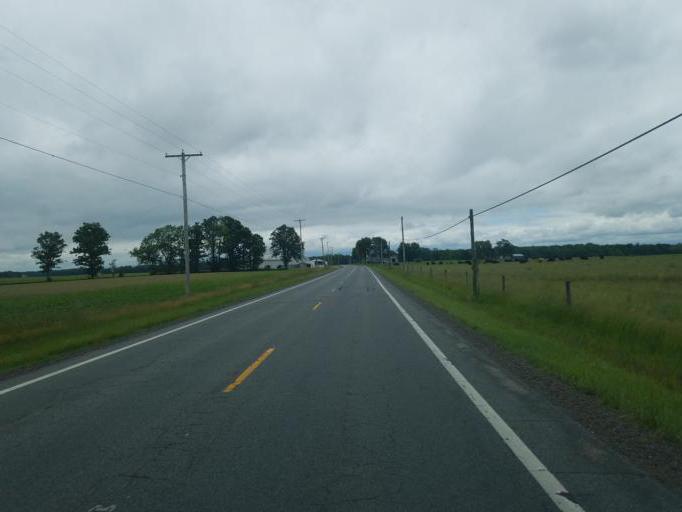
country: US
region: Ohio
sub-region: Crawford County
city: Bucyrus
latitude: 40.7708
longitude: -82.8987
